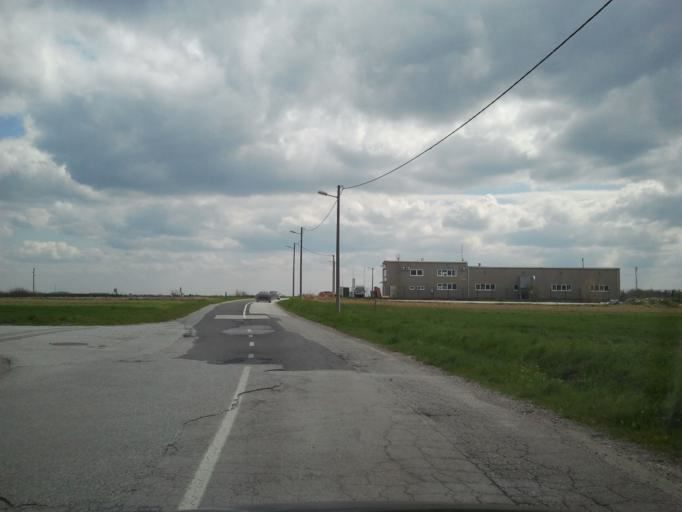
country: HR
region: Grad Zagreb
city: Lucko
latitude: 45.7497
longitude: 15.8544
